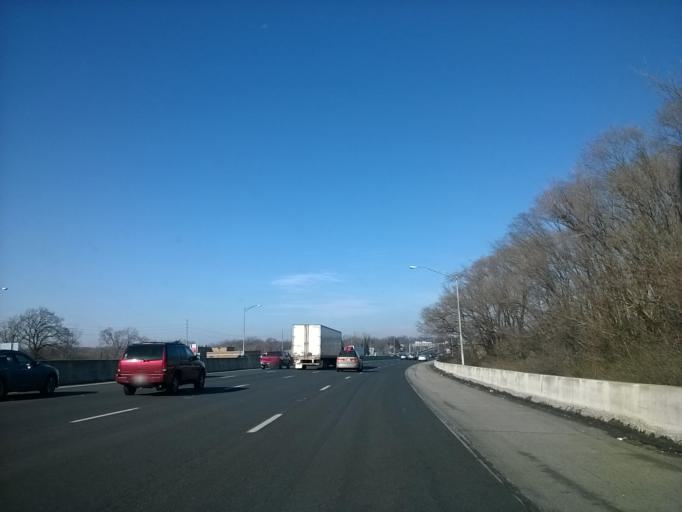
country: US
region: Indiana
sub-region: Marion County
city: Indianapolis
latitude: 39.7985
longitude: -86.1655
